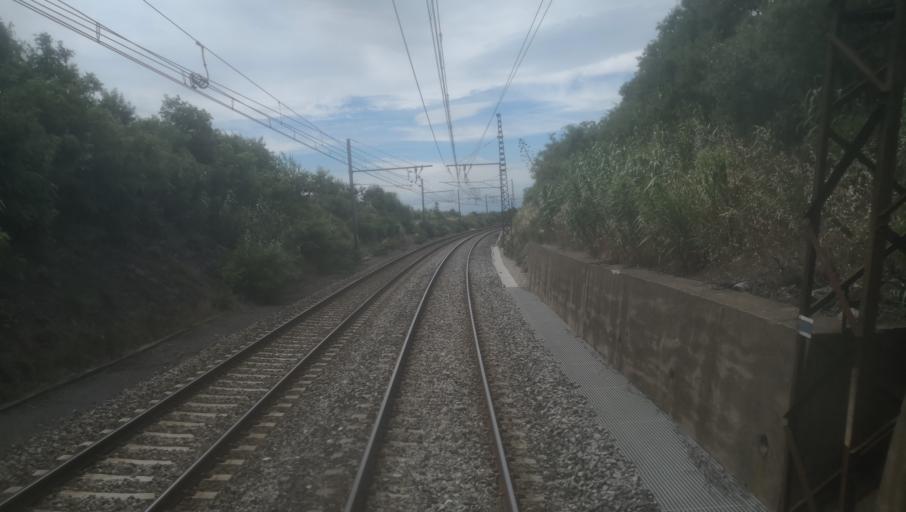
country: FR
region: Languedoc-Roussillon
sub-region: Departement de l'Herault
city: Cers
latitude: 43.3220
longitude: 3.3144
